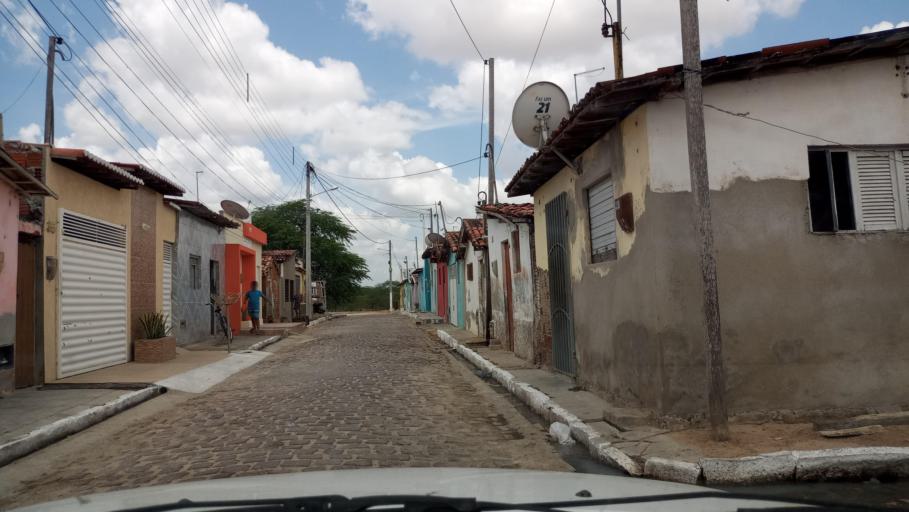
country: BR
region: Rio Grande do Norte
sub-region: Tangara
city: Tangara
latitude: -6.1038
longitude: -35.7134
